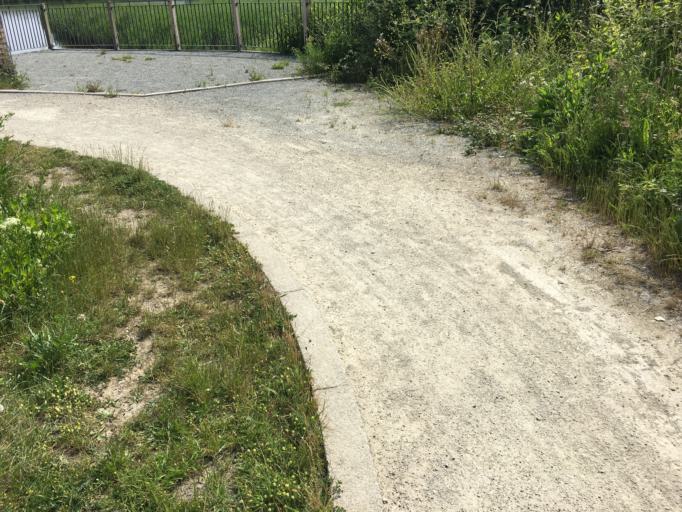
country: GB
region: England
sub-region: Kent
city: Sittingbourne
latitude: 51.3483
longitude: 0.7426
